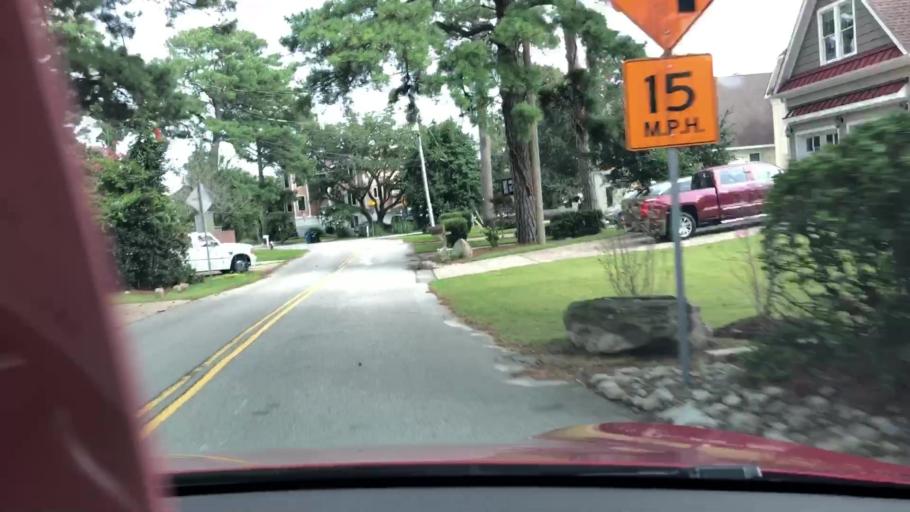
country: US
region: Virginia
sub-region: City of Virginia Beach
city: Virginia Beach
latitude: 36.9066
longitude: -76.0781
